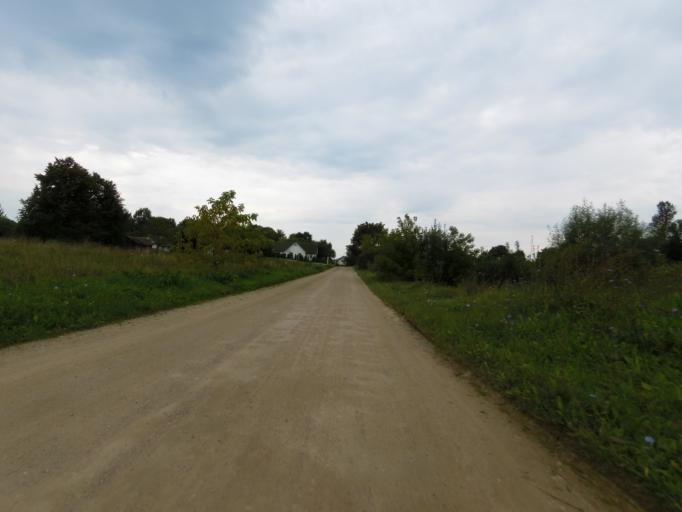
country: LT
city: Grigiskes
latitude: 54.7034
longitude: 25.1271
